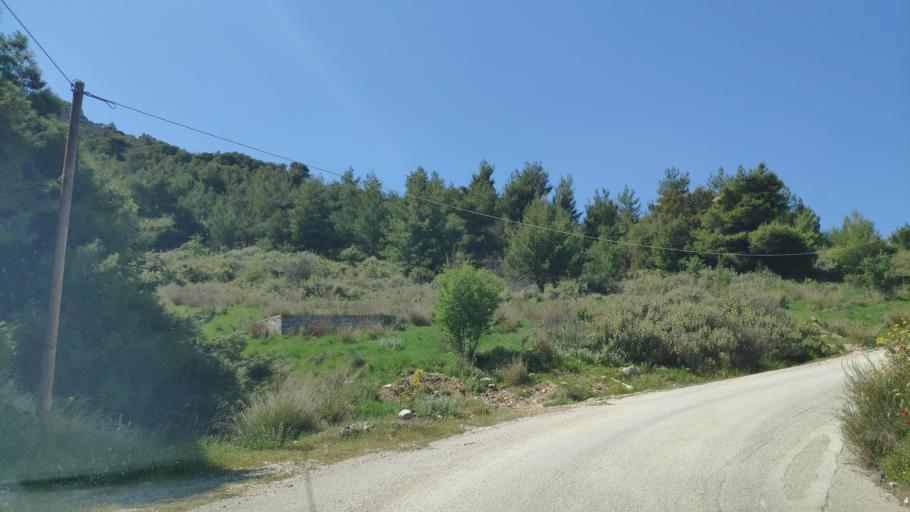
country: GR
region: Attica
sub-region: Nomarchia Athinas
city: Skaramangas
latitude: 38.0292
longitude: 23.6326
